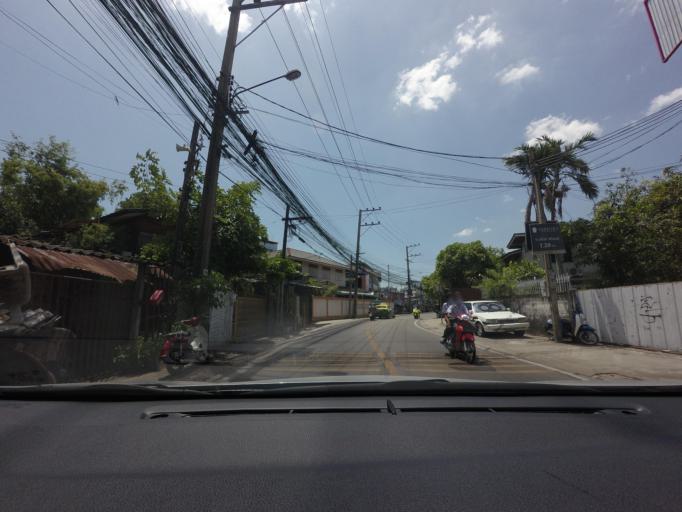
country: TH
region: Bangkok
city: Watthana
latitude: 13.7274
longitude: 100.6126
